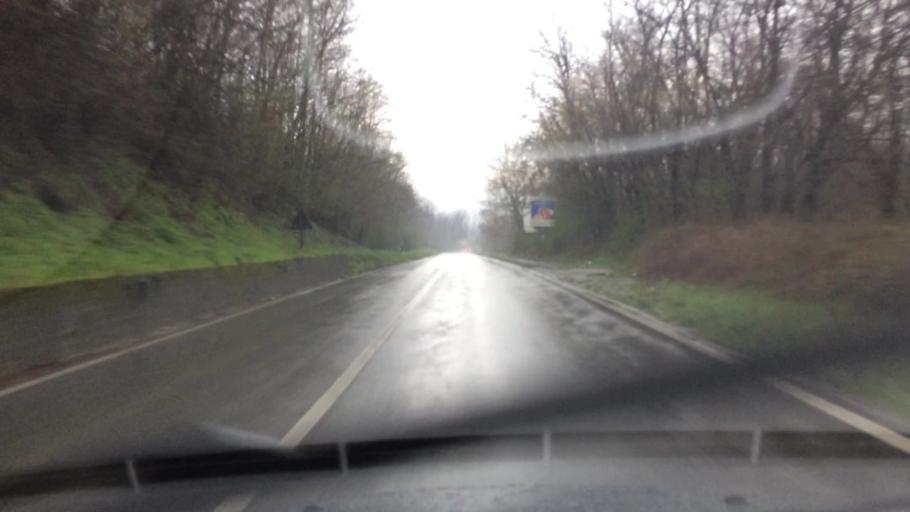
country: IT
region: Lombardy
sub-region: Provincia di Como
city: Montesolaro
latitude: 45.7256
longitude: 9.1070
